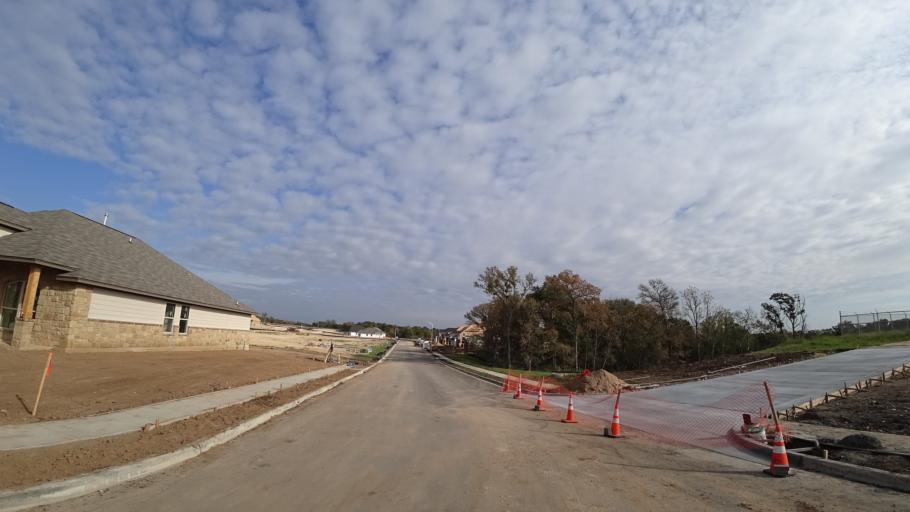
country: US
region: Texas
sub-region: Travis County
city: Manchaca
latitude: 30.1286
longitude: -97.8445
